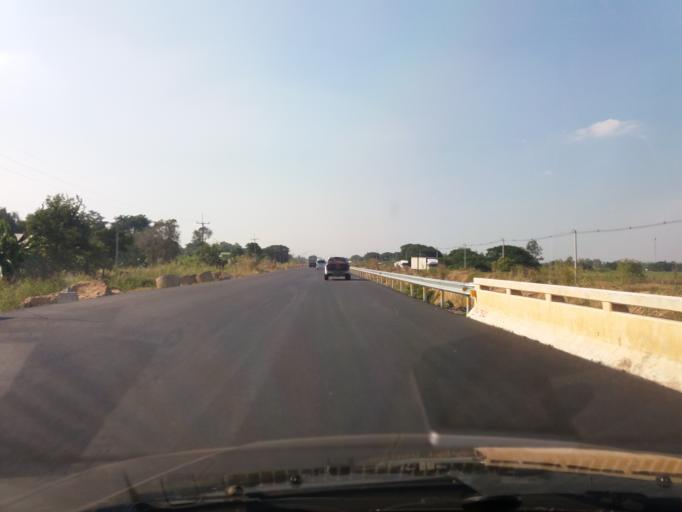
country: TH
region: Nakhon Sawan
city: Krok Phra
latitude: 15.6263
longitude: 100.1092
